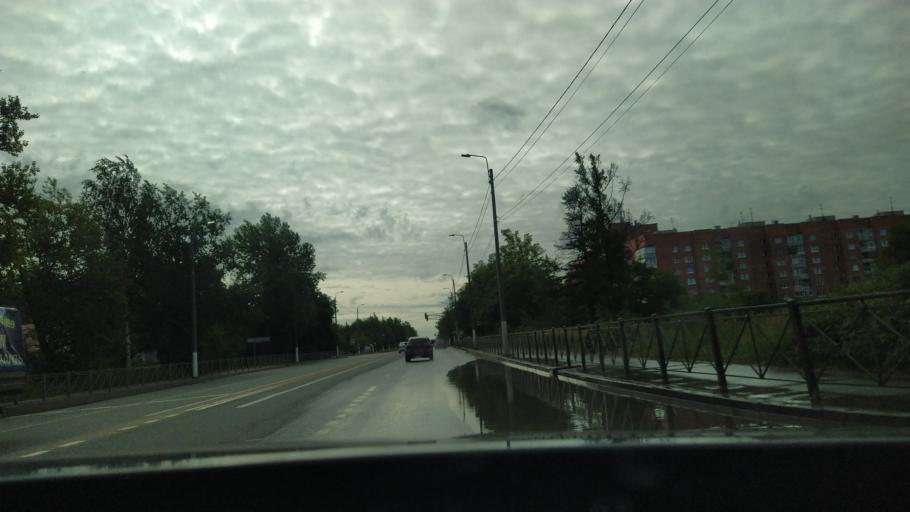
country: RU
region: Leningrad
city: Tosno
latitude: 59.5488
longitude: 30.8627
